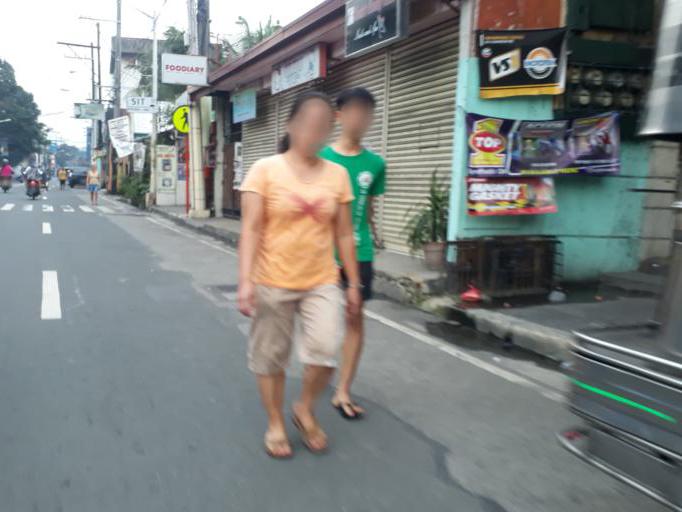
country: PH
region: Metro Manila
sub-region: Caloocan City
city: Niugan
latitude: 14.6558
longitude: 120.9719
